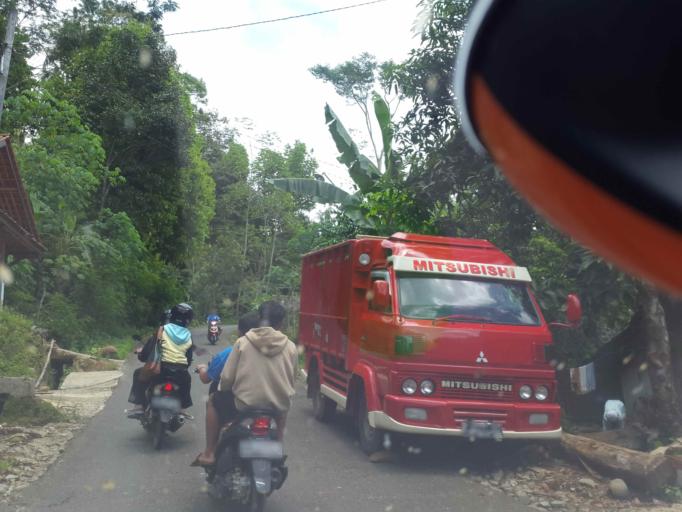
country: ID
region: Central Java
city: Purbalingga
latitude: -7.3549
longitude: 109.6312
